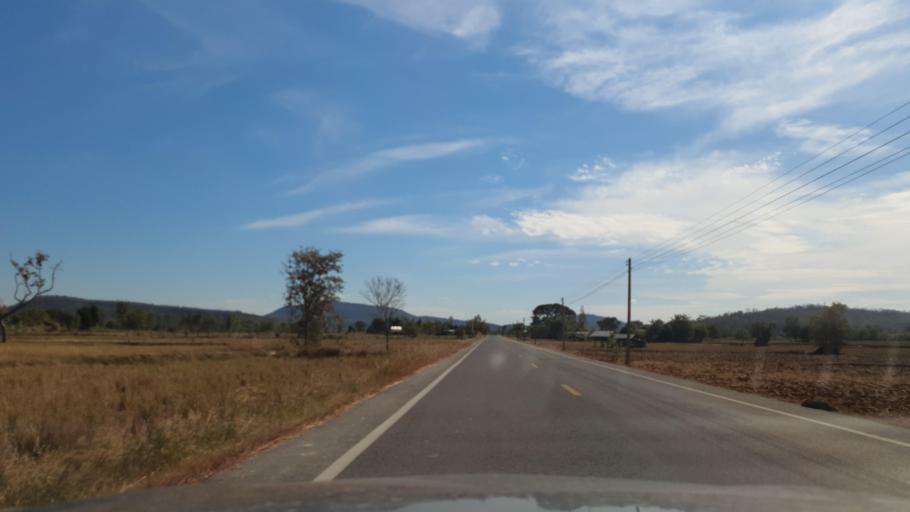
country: TH
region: Kalasin
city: Khao Wong
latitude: 16.6151
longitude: 104.1357
